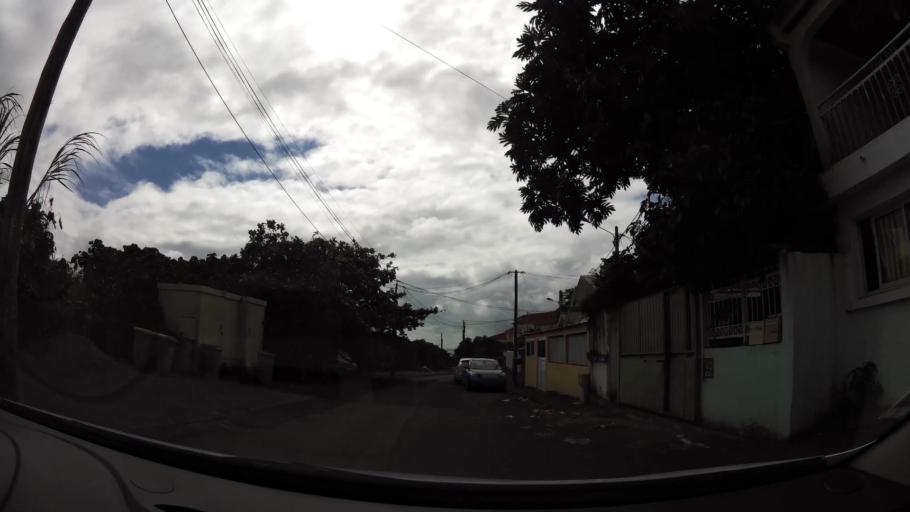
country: RE
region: Reunion
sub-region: Reunion
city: Sainte-Marie
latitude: -20.9025
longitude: 55.5668
